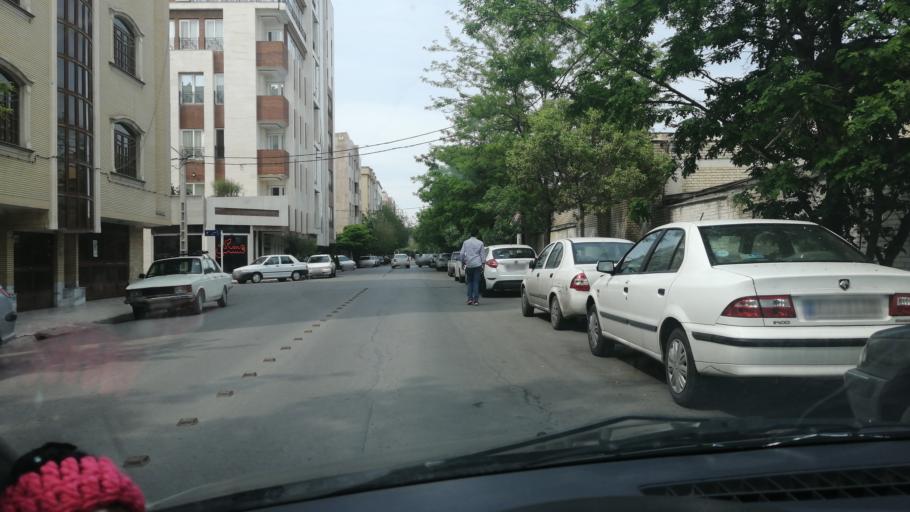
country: IR
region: Razavi Khorasan
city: Mashhad
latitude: 36.3251
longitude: 59.5669
